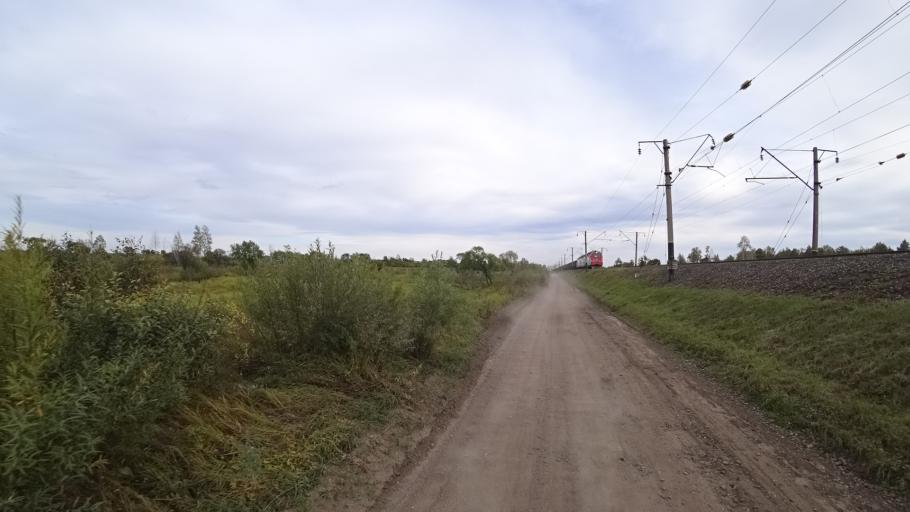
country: RU
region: Amur
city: Arkhara
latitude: 49.3562
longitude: 130.1538
